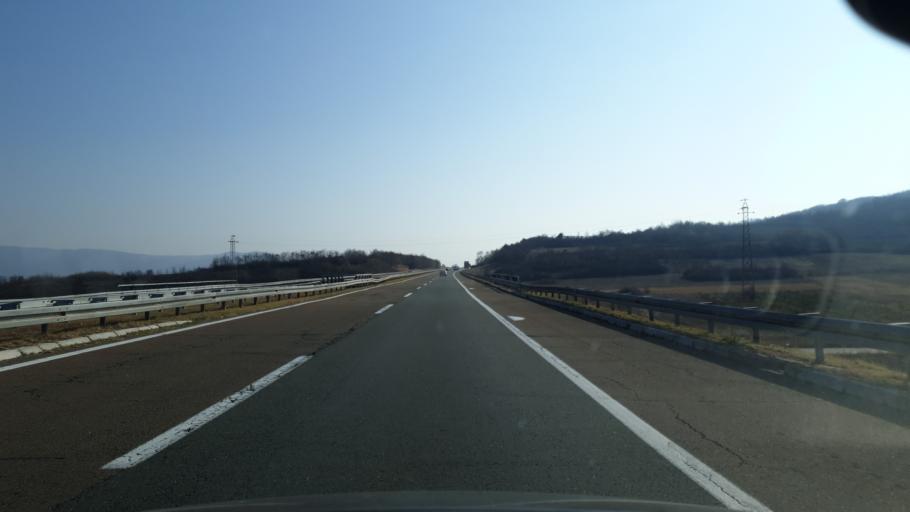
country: RS
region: Central Serbia
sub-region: Nisavski Okrug
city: Doljevac
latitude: 43.2702
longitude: 21.8073
